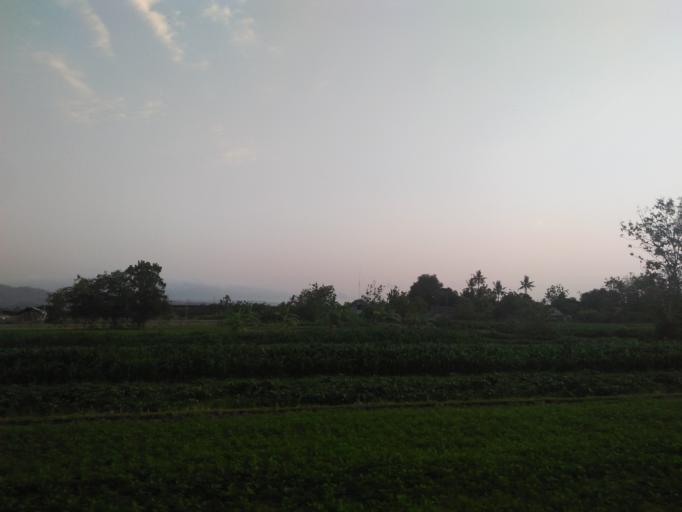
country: ID
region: Daerah Istimewa Yogyakarta
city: Sewon
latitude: -7.8570
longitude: 110.4147
